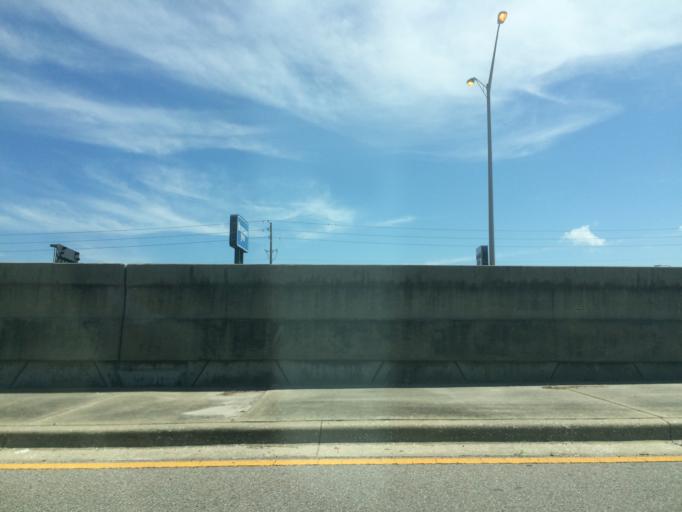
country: US
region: Florida
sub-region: Pinellas County
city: South Highpoint
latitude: 27.9214
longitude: -82.7306
